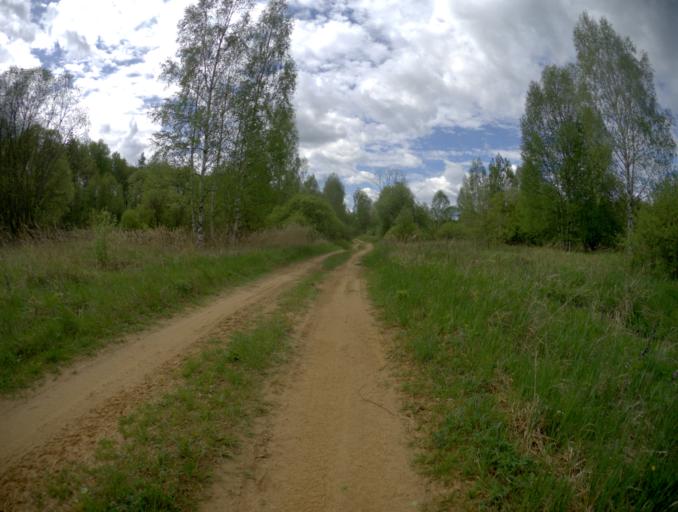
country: RU
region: Moskovskaya
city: Cherusti
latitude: 55.4832
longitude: 40.0396
